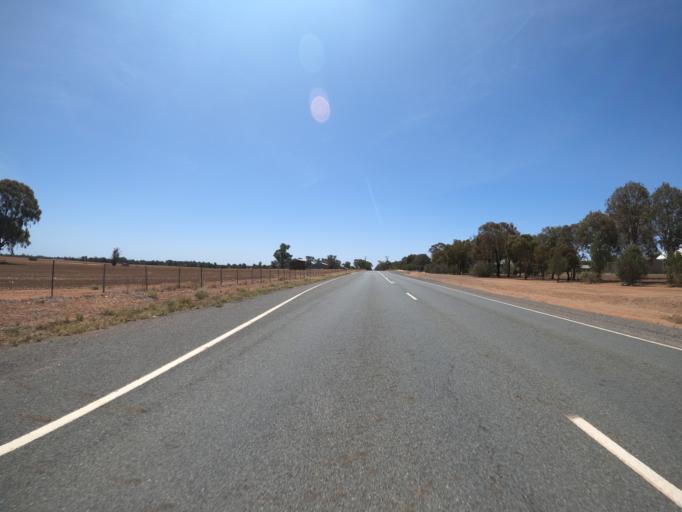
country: AU
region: Victoria
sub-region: Moira
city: Yarrawonga
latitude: -36.0496
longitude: 145.9955
